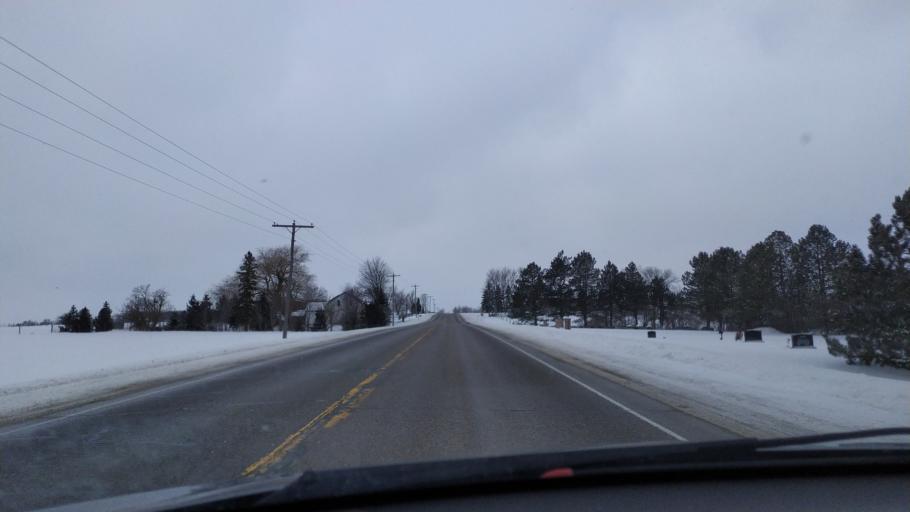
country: CA
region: Ontario
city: North Perth
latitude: 43.5755
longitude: -80.8437
